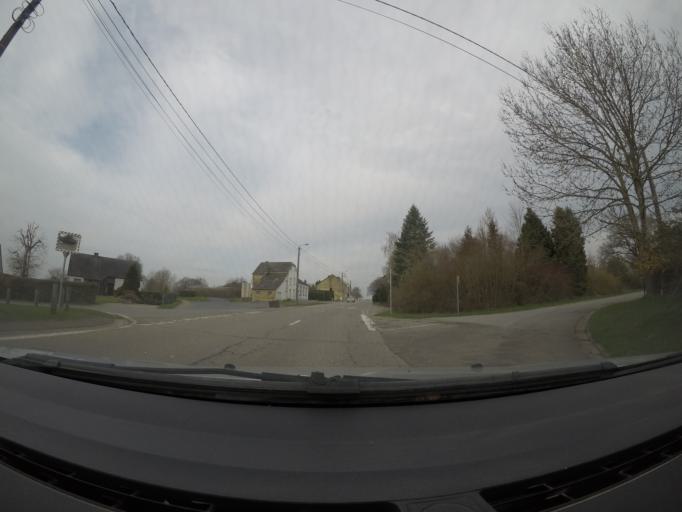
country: BE
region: Wallonia
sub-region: Province du Luxembourg
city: Tintigny
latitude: 49.7159
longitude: 5.5196
